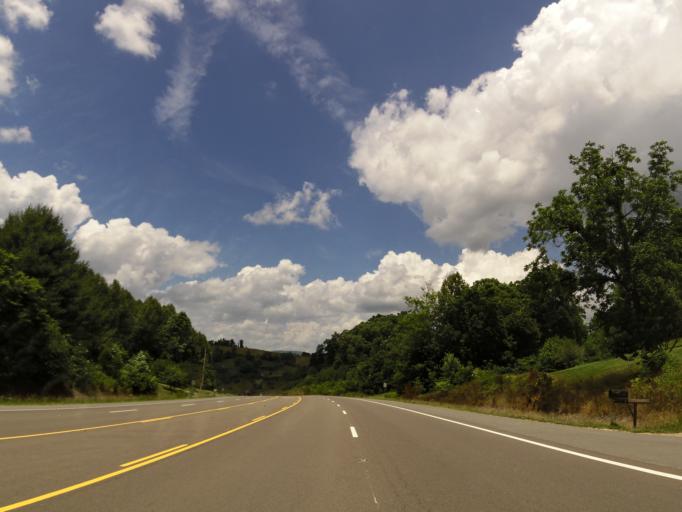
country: US
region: Tennessee
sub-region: Claiborne County
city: Harrogate
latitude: 36.5283
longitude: -83.6163
